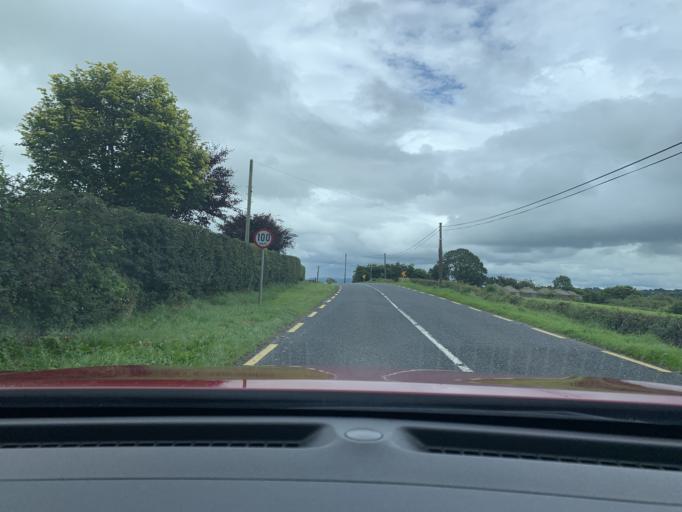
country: IE
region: Ulster
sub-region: County Donegal
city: Convoy
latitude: 54.7978
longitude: -7.6648
